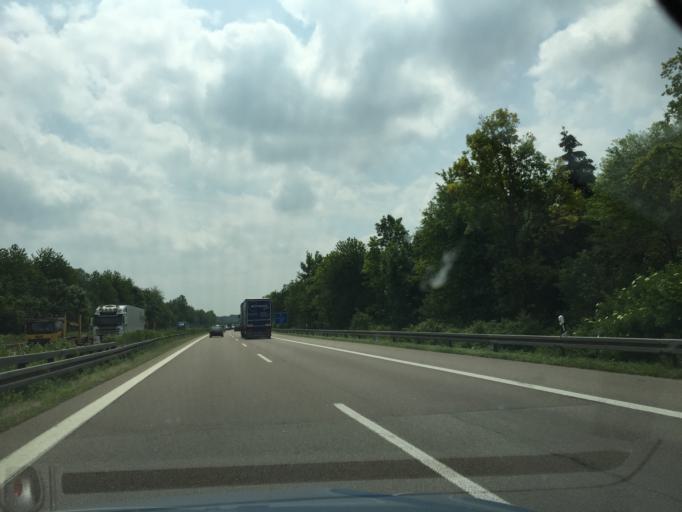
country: DE
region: Bavaria
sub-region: Swabia
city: Nersingen
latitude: 48.4379
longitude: 10.1092
